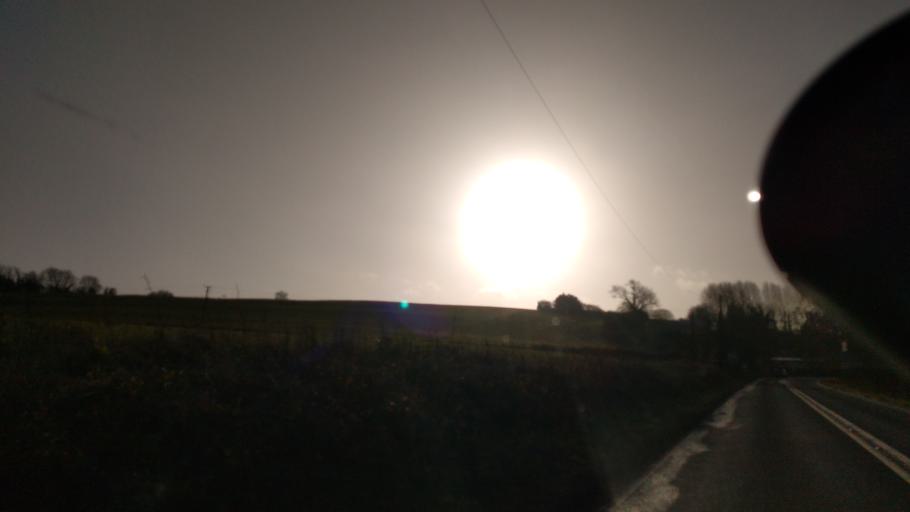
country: GB
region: England
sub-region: Somerset
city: Evercreech
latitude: 51.1425
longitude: -2.5485
